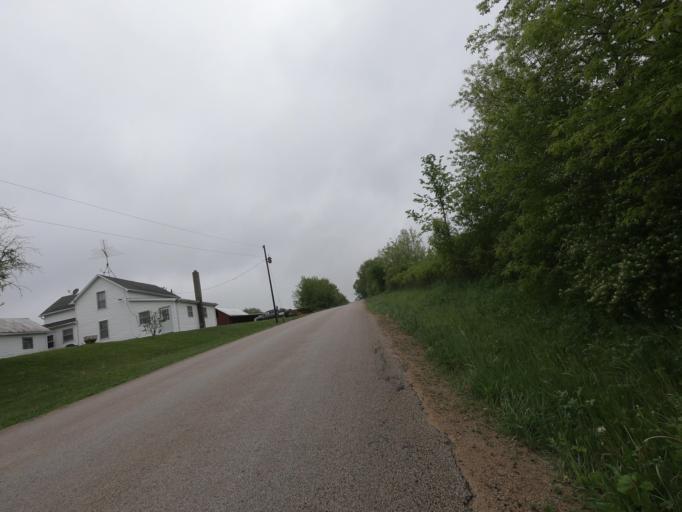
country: US
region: Wisconsin
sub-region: Grant County
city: Hazel Green
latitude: 42.4837
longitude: -90.4891
